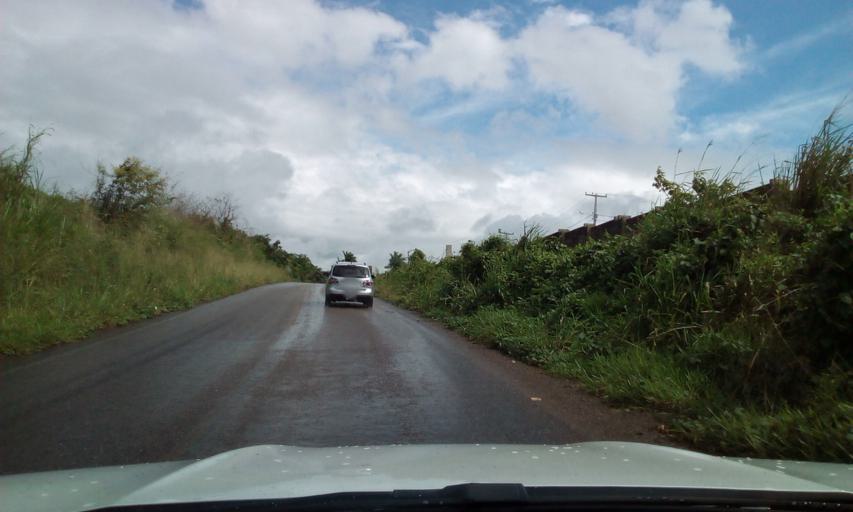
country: BR
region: Paraiba
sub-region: Areia
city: Areia
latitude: -6.9462
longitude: -35.6655
